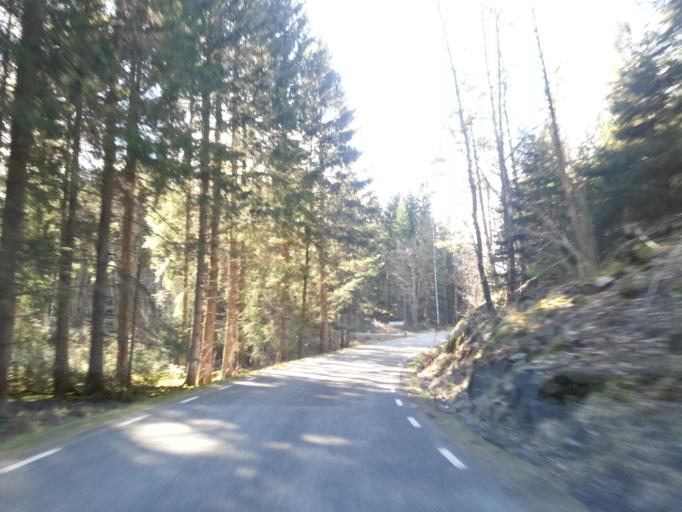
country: SE
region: Vaestra Goetaland
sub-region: Kungalvs Kommun
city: Diserod
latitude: 57.9634
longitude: 12.0023
